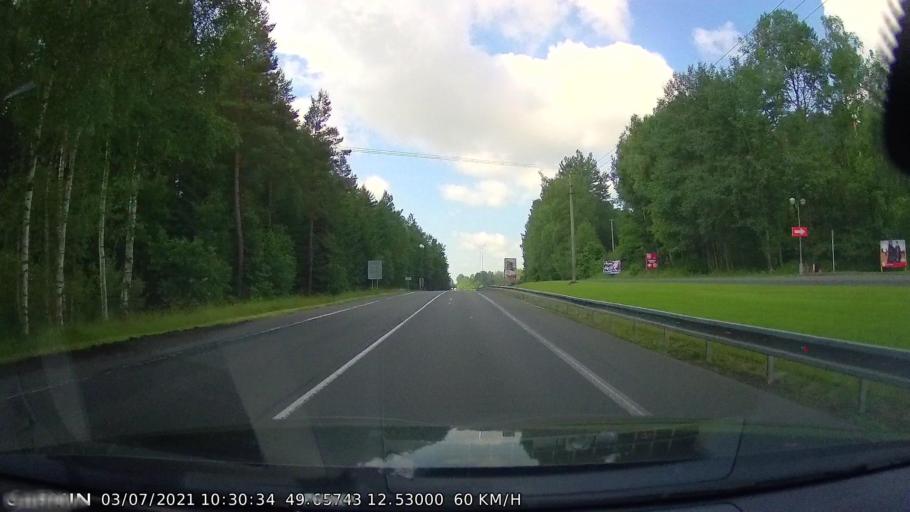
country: DE
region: Bavaria
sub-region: Upper Palatinate
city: Waidhaus
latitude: 49.6574
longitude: 12.5301
